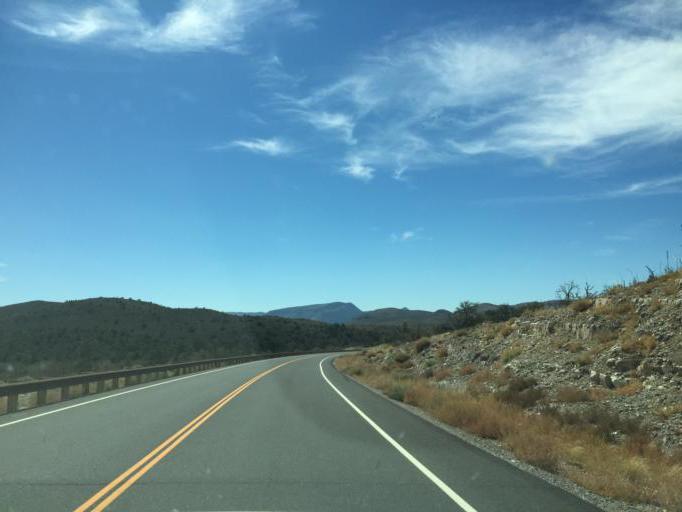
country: US
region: Arizona
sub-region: Mohave County
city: Meadview
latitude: 35.9243
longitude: -113.9101
